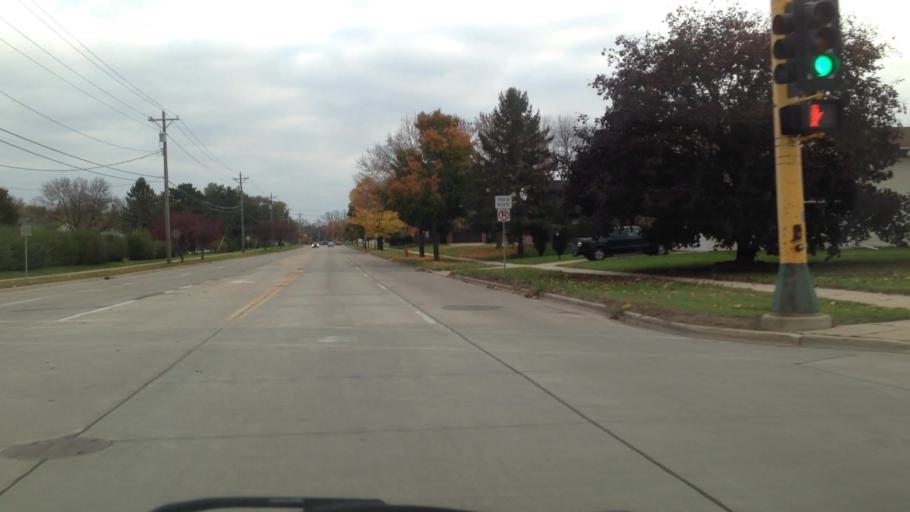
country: US
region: Minnesota
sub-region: Olmsted County
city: Rochester
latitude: 44.0144
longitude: -92.4453
